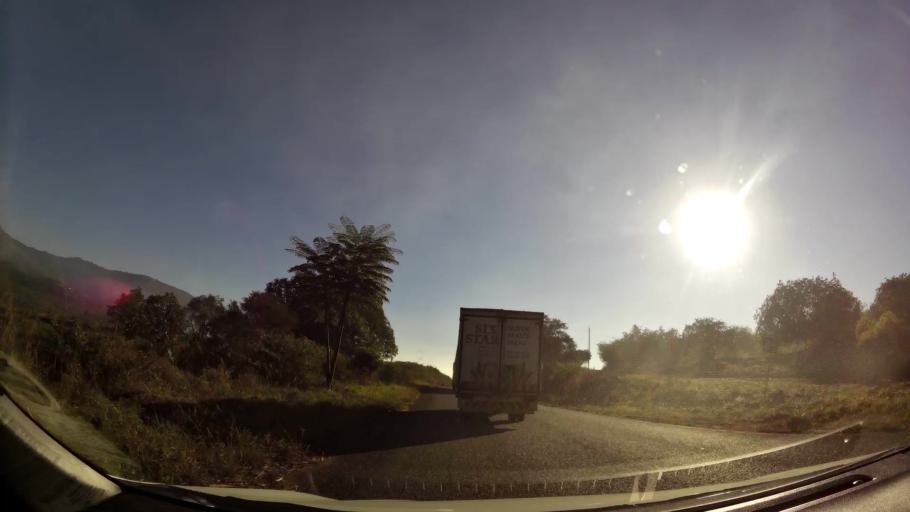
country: ZA
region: Limpopo
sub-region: Mopani District Municipality
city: Tzaneen
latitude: -23.8958
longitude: 30.0750
